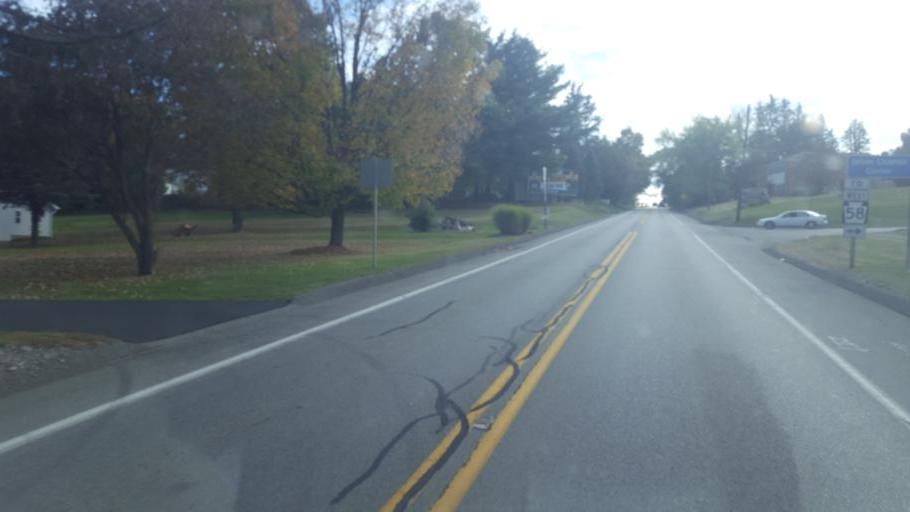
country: US
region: Pennsylvania
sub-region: Mercer County
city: Mercer
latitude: 41.2327
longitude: -80.2389
